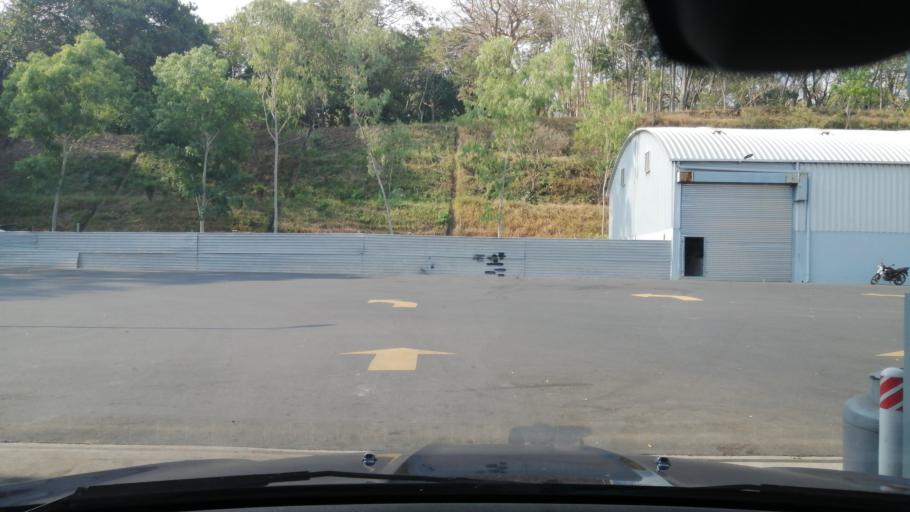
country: SV
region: Santa Ana
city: Santa Ana
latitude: 13.9541
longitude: -89.5644
